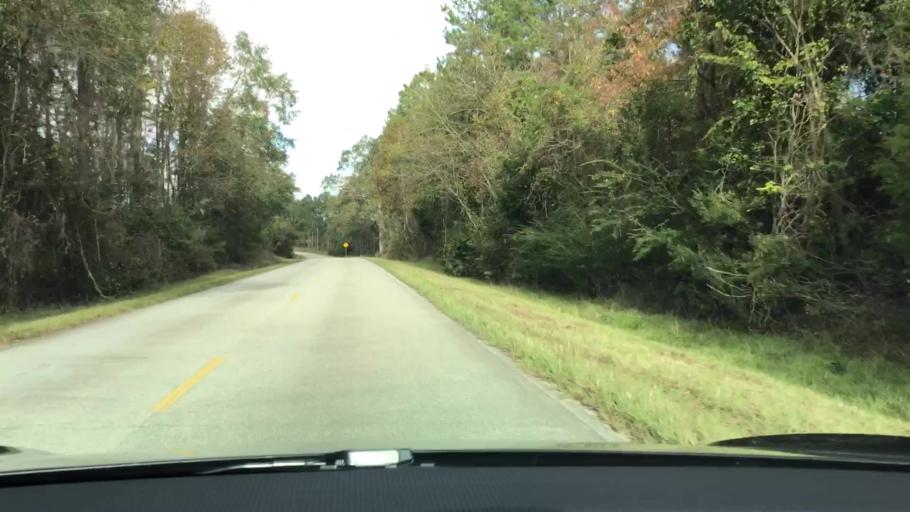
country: US
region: Georgia
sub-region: Jefferson County
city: Wadley
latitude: 32.8037
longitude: -82.3875
